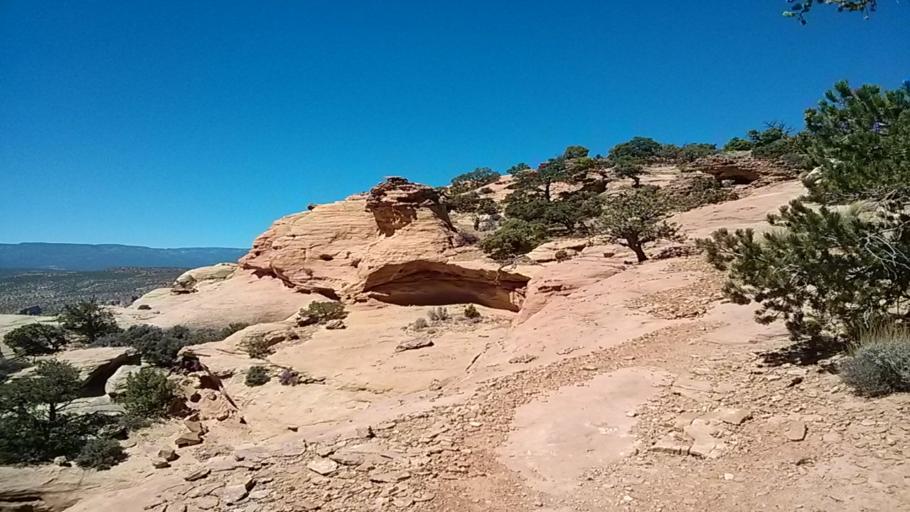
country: US
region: Utah
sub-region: Wayne County
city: Loa
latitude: 38.3055
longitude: -111.2687
